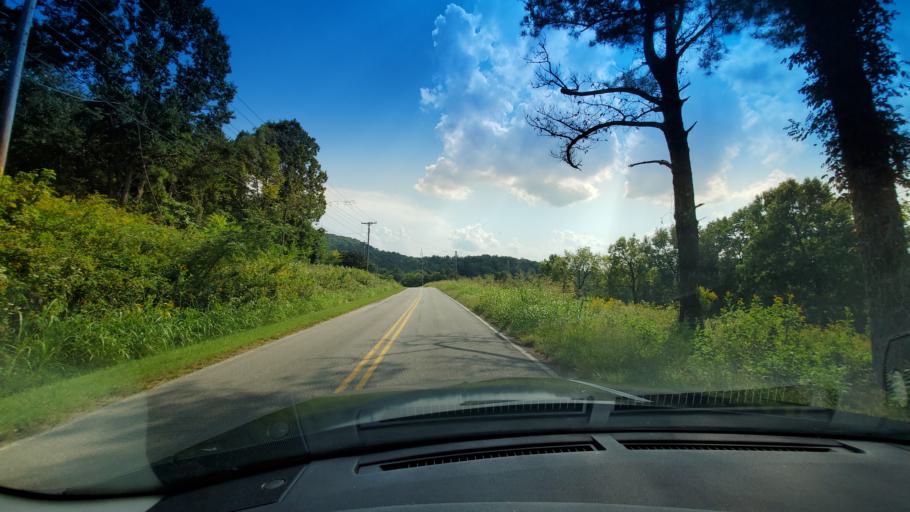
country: US
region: Tennessee
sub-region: Smith County
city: Carthage
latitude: 36.2494
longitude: -85.9661
